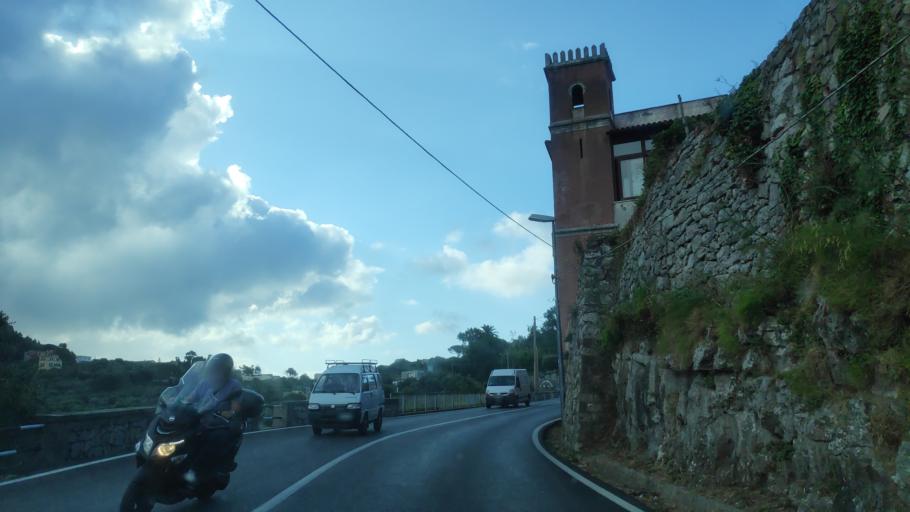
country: IT
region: Campania
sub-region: Provincia di Napoli
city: Piano di Sorrento
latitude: 40.6202
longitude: 14.4225
